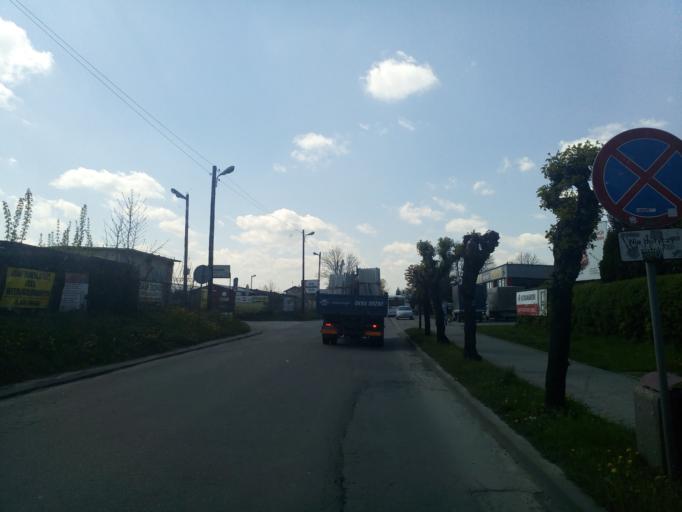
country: PL
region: Lesser Poland Voivodeship
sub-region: Powiat nowosadecki
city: Nowy Sacz
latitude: 49.6085
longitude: 20.7067
